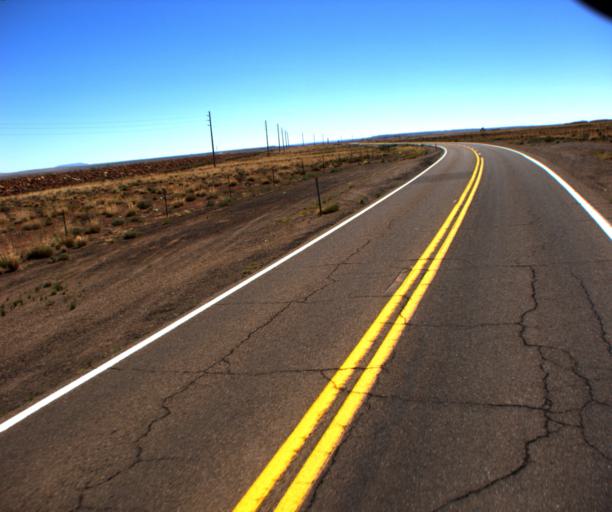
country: US
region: Arizona
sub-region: Navajo County
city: Winslow
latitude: 35.0058
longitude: -110.7010
